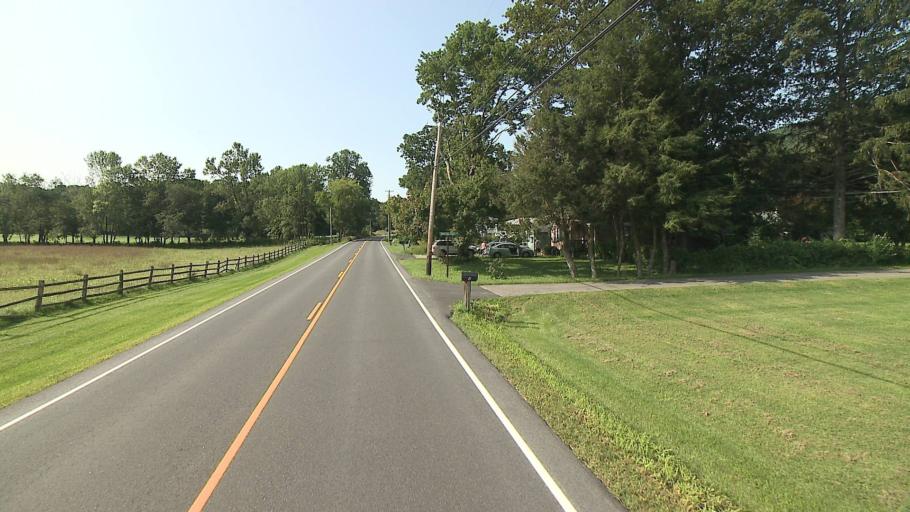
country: US
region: Connecticut
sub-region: Litchfield County
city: Kent
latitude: 41.7034
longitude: -73.4910
